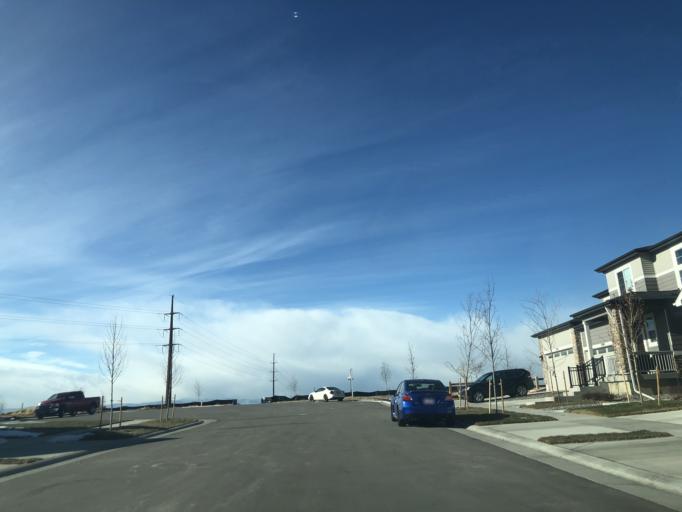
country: US
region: Colorado
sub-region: Douglas County
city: Stonegate
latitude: 39.5546
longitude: -104.8065
